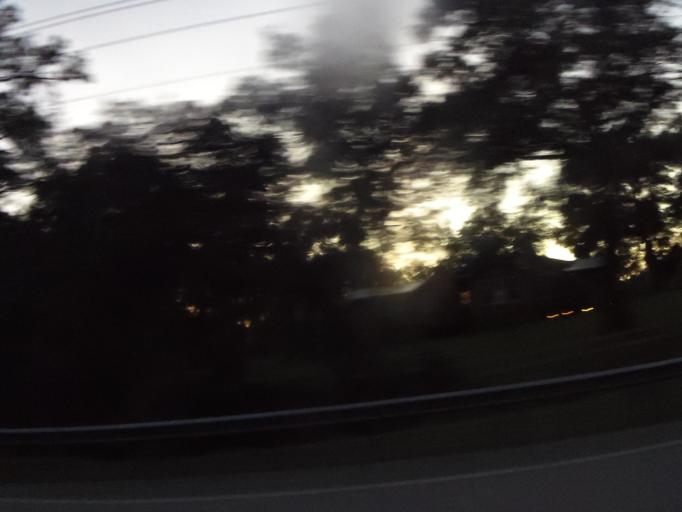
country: US
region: Florida
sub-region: Saint Johns County
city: Saint Augustine Shores
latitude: 29.8212
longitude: -81.3470
